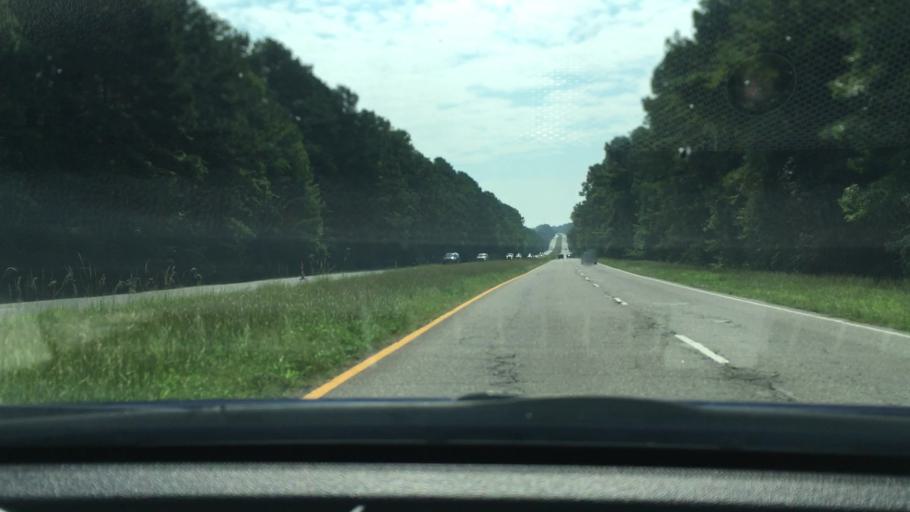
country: US
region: South Carolina
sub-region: Sumter County
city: Stateburg
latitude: 33.9522
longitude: -80.5619
